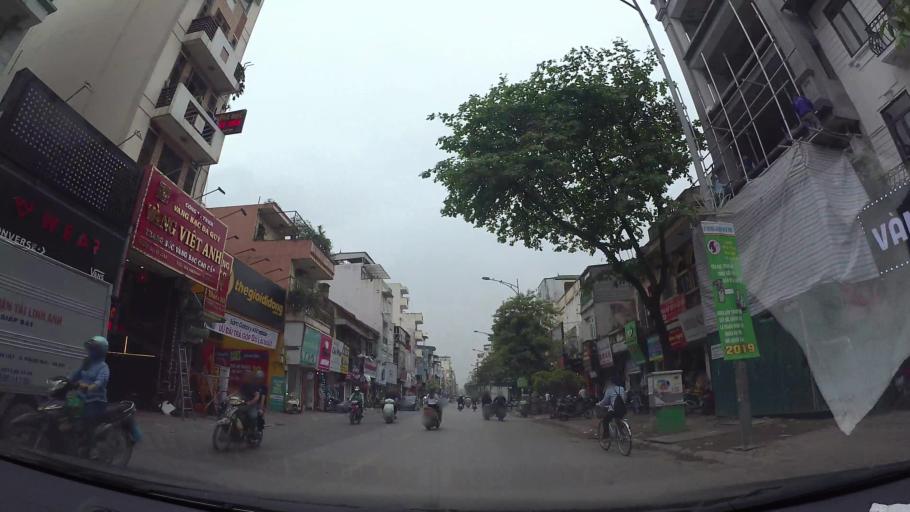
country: VN
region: Ha Noi
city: Hai BaTrung
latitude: 20.9979
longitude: 105.8502
